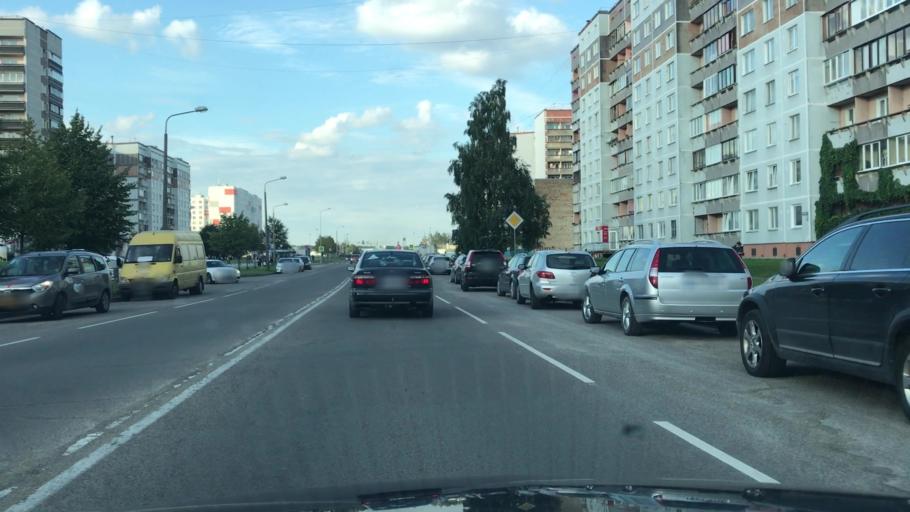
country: LV
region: Stopini
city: Ulbroka
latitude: 56.9422
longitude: 24.2164
